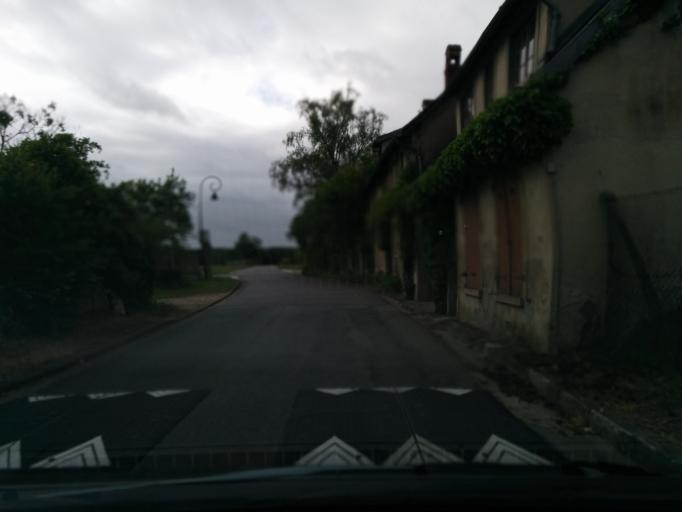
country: FR
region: Ile-de-France
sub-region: Departement des Yvelines
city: Rosny-sur-Seine
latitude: 49.0332
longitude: 1.6483
